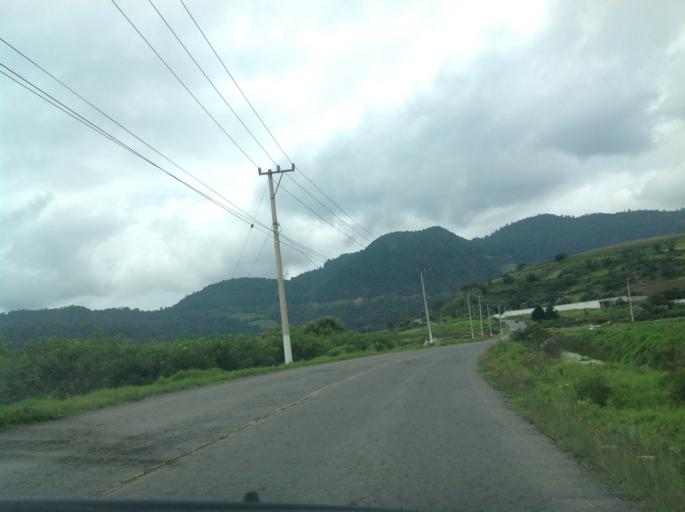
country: MX
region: Mexico
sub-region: Tenango del Valle
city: Santa Maria Jajalpa
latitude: 19.1092
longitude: -99.5306
